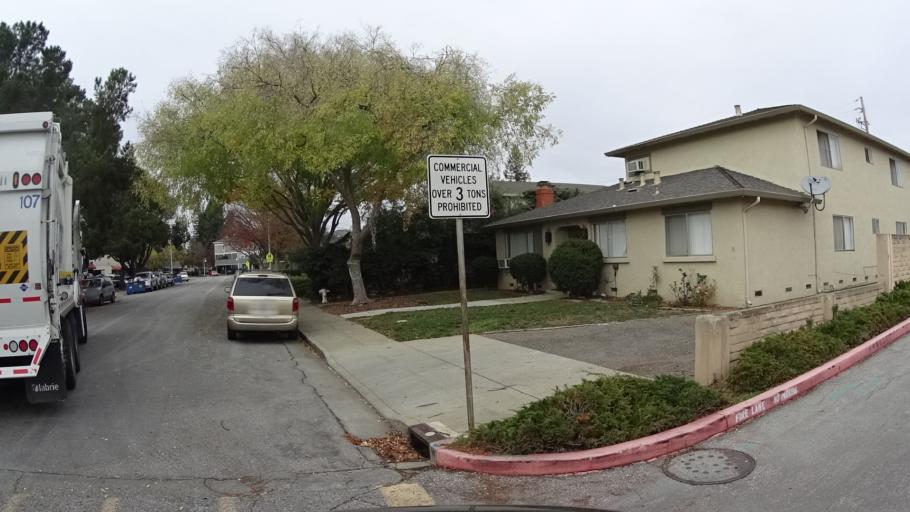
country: US
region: California
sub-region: Santa Clara County
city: Sunnyvale
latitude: 37.3656
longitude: -122.0157
